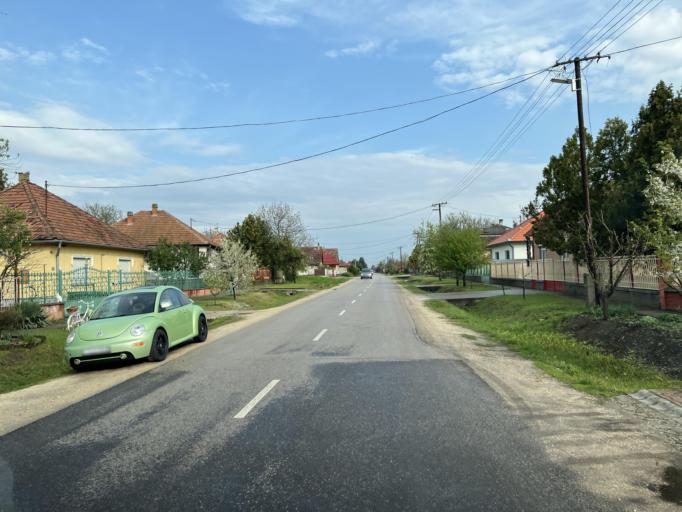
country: HU
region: Pest
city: Nyaregyhaza
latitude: 47.2226
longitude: 19.4583
